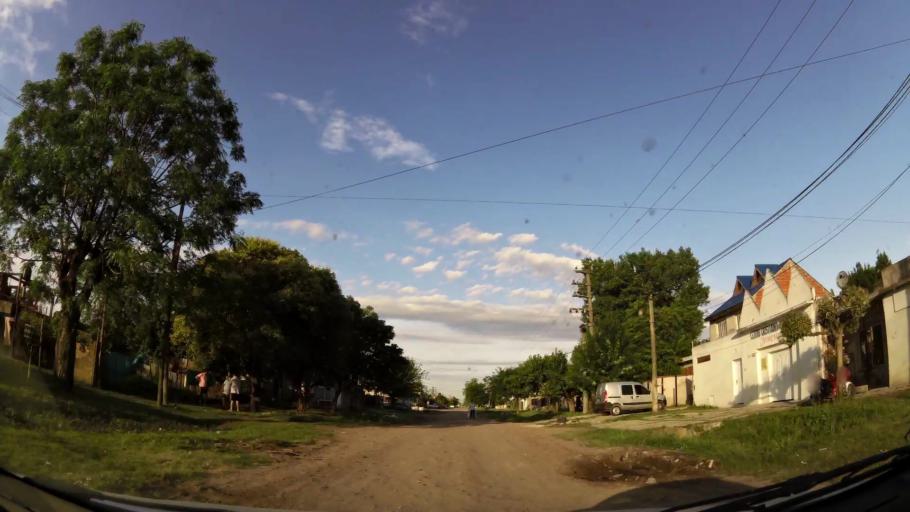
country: AR
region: Buenos Aires
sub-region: Partido de Merlo
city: Merlo
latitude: -34.6926
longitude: -58.7480
